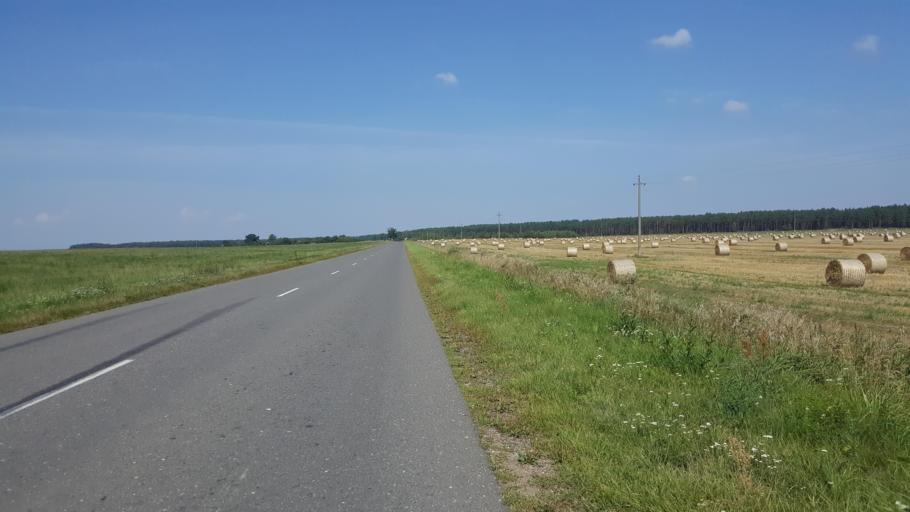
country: BY
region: Brest
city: Kamyanyuki
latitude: 52.4962
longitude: 23.6751
